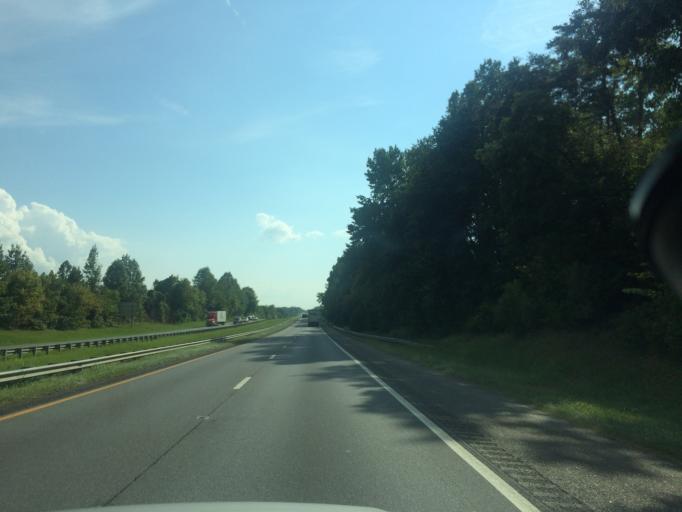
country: US
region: North Carolina
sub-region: Cleveland County
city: Kings Mountain
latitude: 35.2184
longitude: -81.3434
